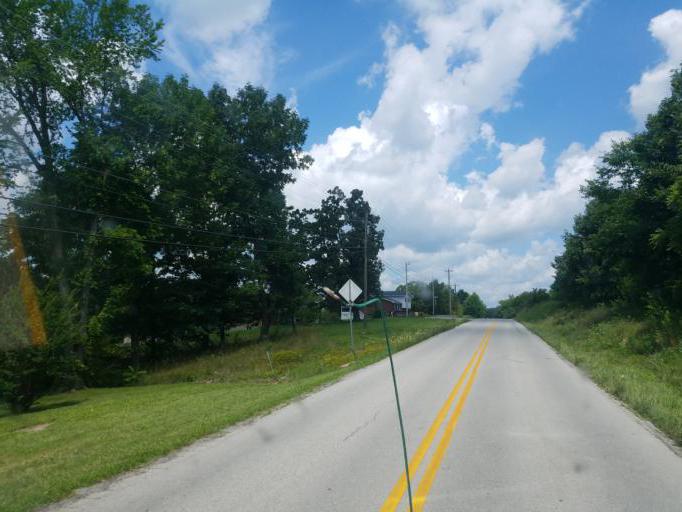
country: US
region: Kentucky
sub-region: Grayson County
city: Leitchfield
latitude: 37.5013
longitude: -86.3111
